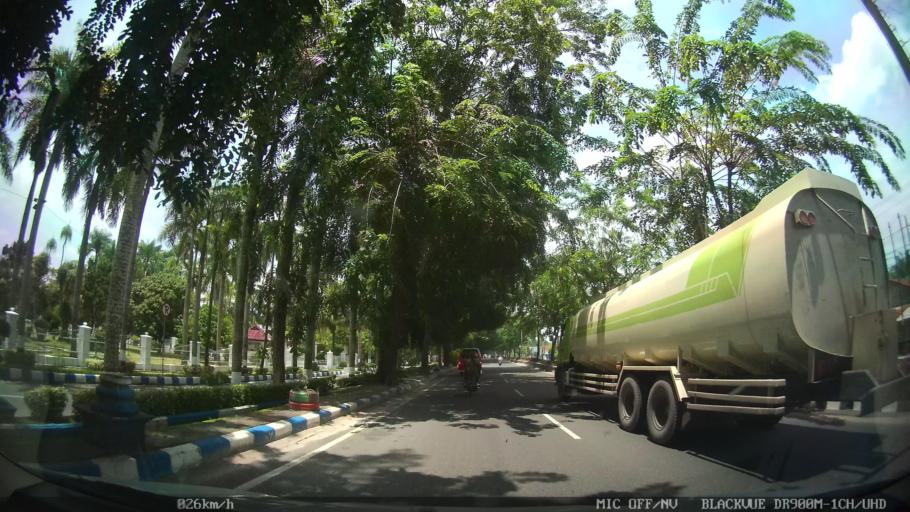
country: ID
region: North Sumatra
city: Percut
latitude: 3.5518
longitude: 98.8686
